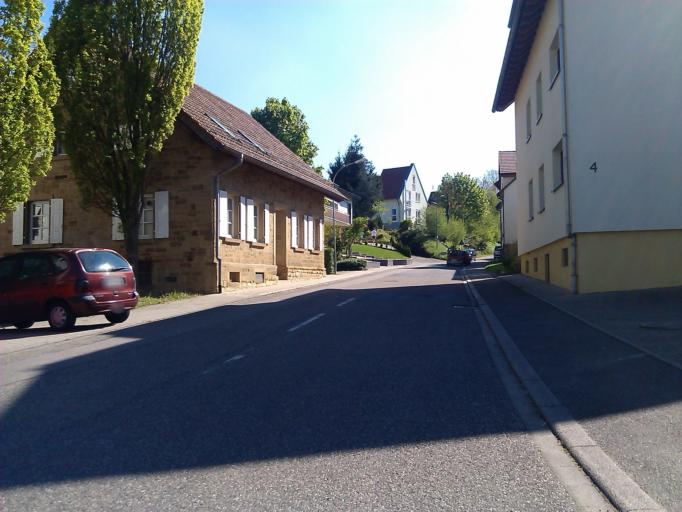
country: DE
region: Baden-Wuerttemberg
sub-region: Karlsruhe Region
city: Kurnbach
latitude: 49.0764
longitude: 8.8439
